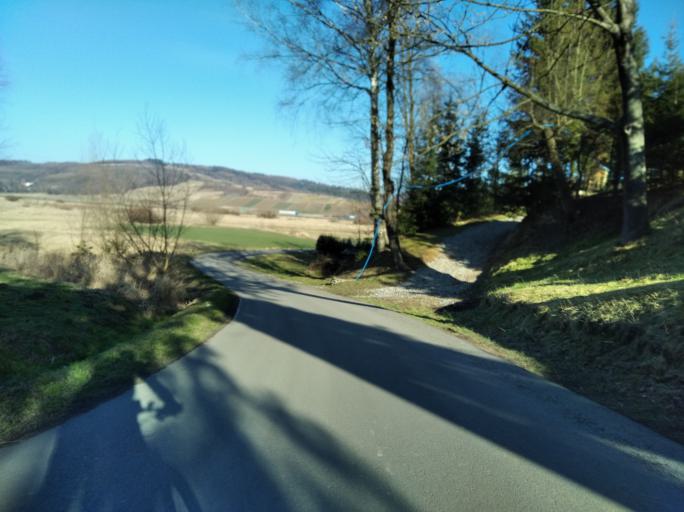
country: PL
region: Subcarpathian Voivodeship
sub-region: Powiat brzozowski
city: Domaradz
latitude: 49.7956
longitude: 21.9294
